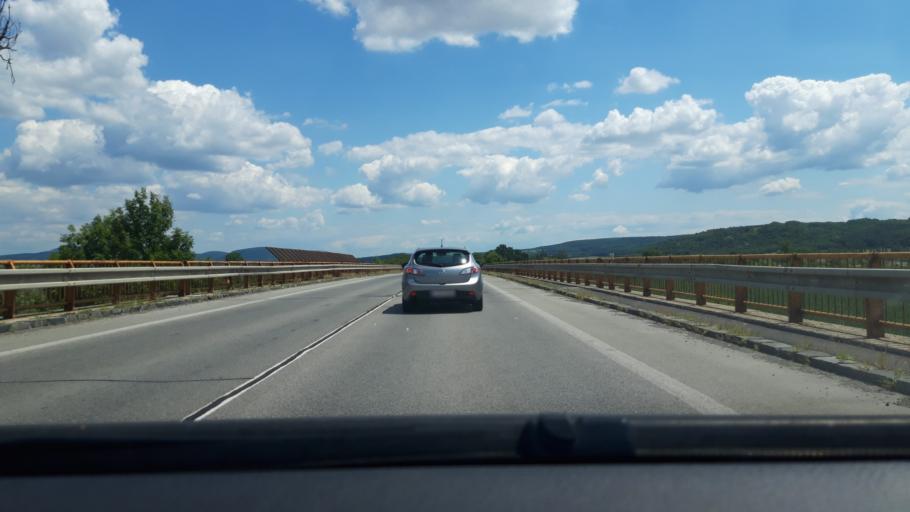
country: SK
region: Banskobystricky
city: Lucenec
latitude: 48.3081
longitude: 19.7156
